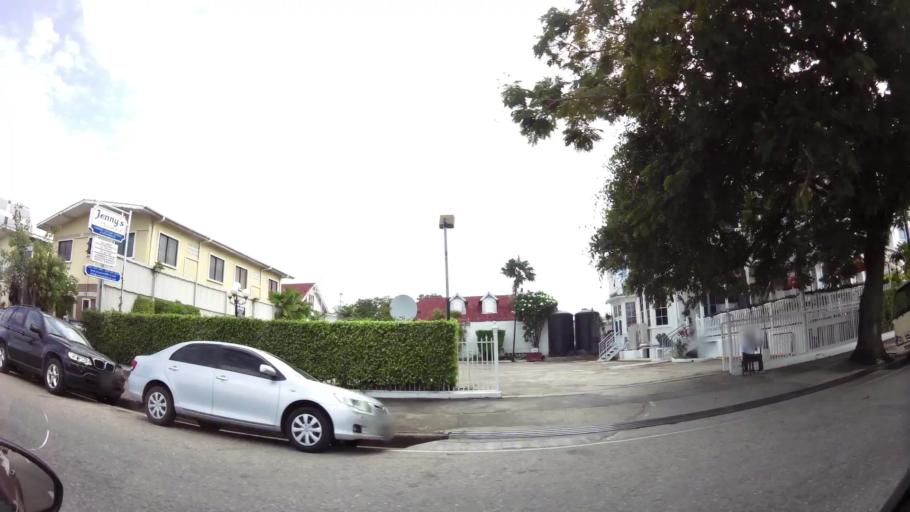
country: TT
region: City of Port of Spain
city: Port-of-Spain
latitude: 10.6613
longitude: -61.5167
